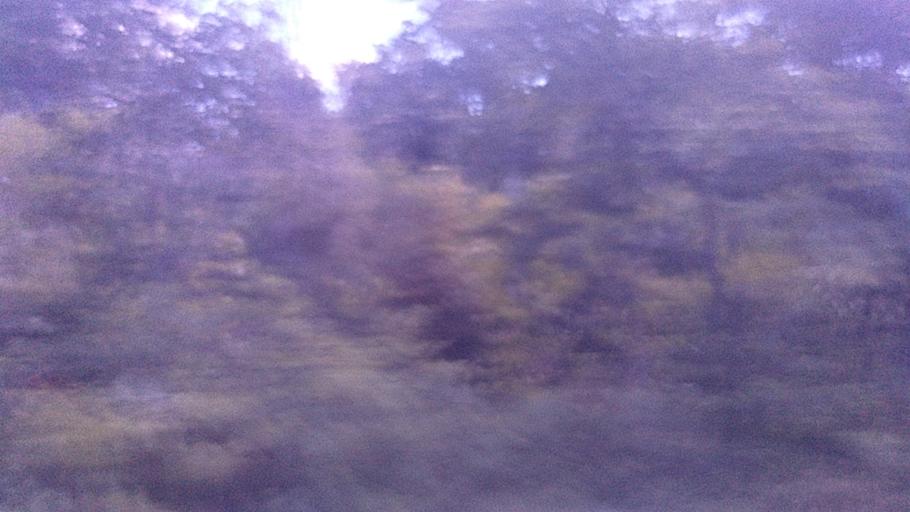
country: TH
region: Chaiyaphum
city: Phu Khiao
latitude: 16.3212
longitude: 102.2023
